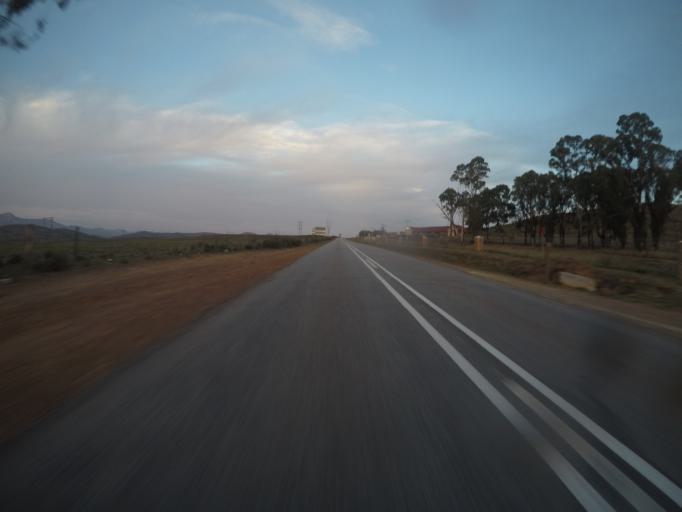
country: ZA
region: Western Cape
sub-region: Eden District Municipality
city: Plettenberg Bay
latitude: -33.7405
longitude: 23.4352
